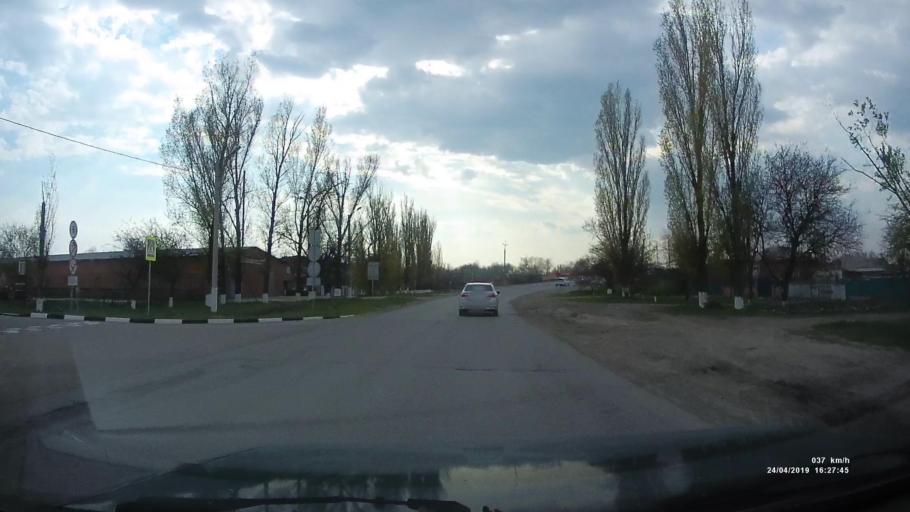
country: RU
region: Rostov
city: Orlovskiy
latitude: 46.8627
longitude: 42.0391
